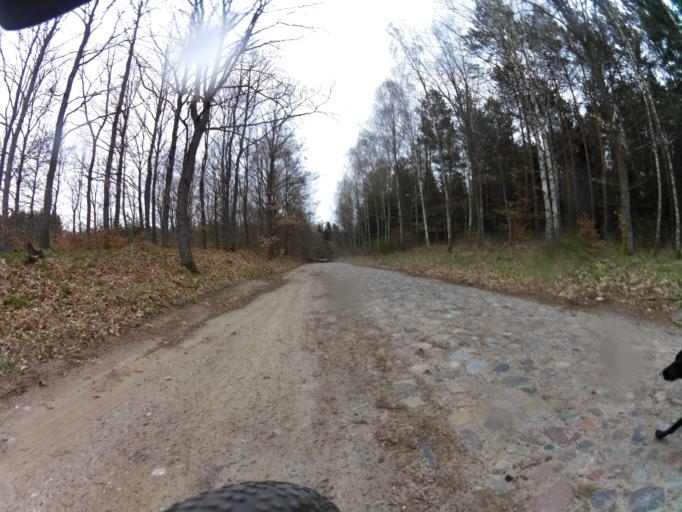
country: PL
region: West Pomeranian Voivodeship
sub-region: Powiat koszalinski
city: Bobolice
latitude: 54.0386
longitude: 16.6144
